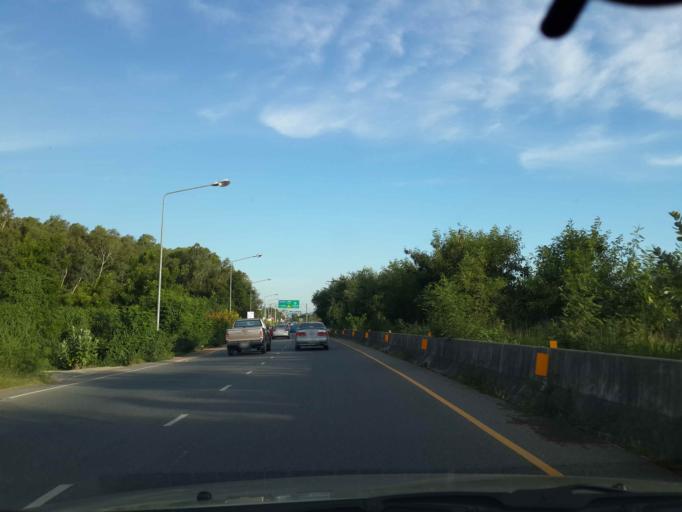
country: TH
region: Chon Buri
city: Phatthaya
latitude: 12.8922
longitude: 100.9005
